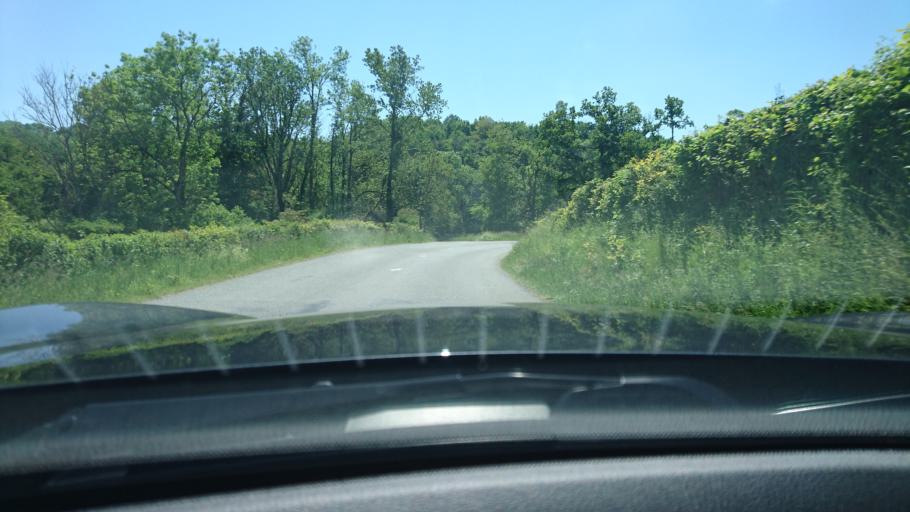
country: FR
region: Rhone-Alpes
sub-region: Departement de la Loire
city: Panissieres
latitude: 45.8085
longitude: 4.3194
